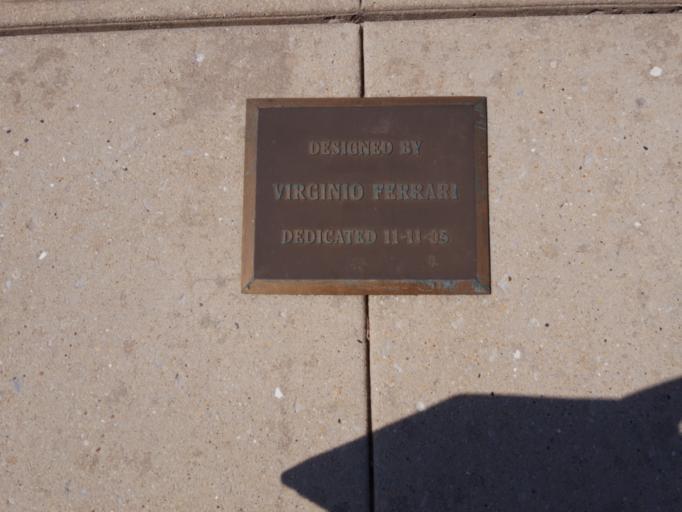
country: US
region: Illinois
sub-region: Cook County
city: Orland Park
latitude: 41.6227
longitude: -87.8573
